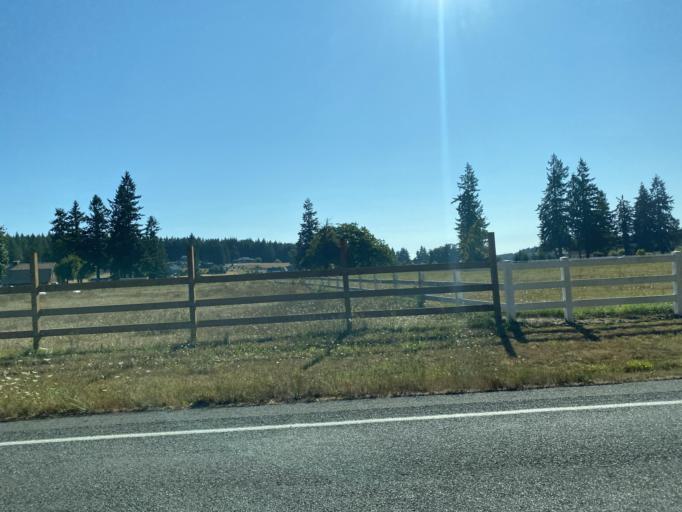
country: US
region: Washington
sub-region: Thurston County
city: Tanglewilde-Thompson Place
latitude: 46.9690
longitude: -122.7645
